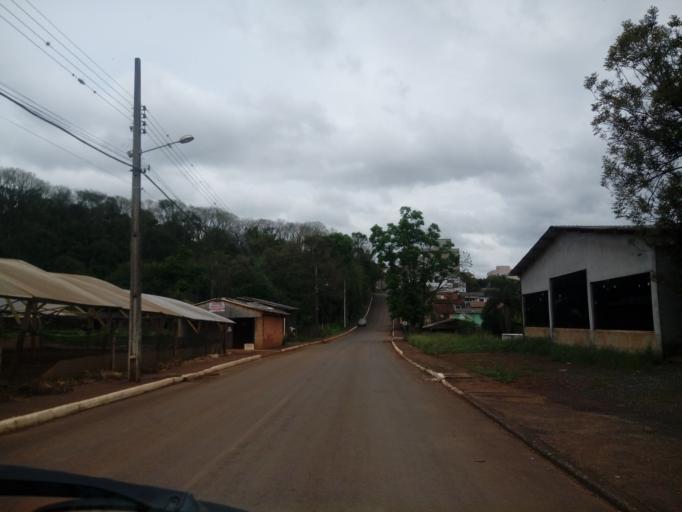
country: BR
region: Santa Catarina
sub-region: Chapeco
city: Chapeco
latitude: -27.0726
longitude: -52.6179
